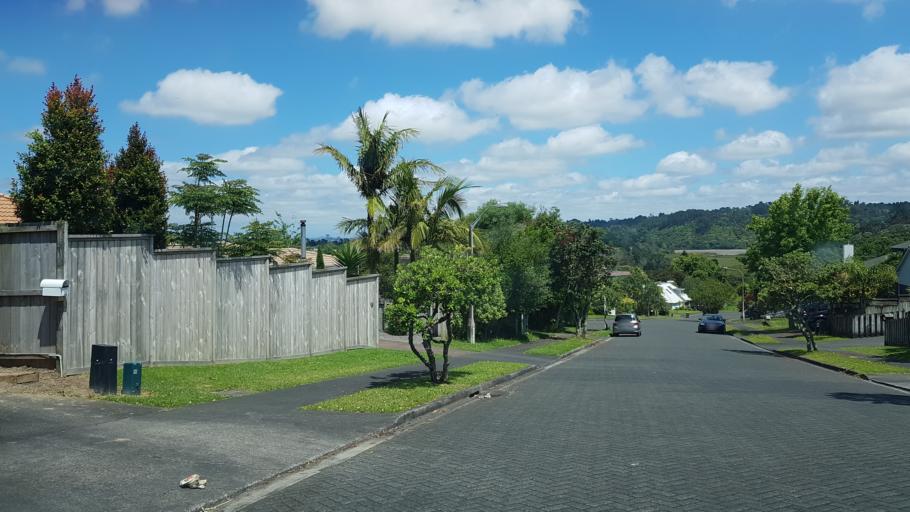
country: NZ
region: Auckland
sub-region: Auckland
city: North Shore
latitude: -36.7875
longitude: 174.7081
